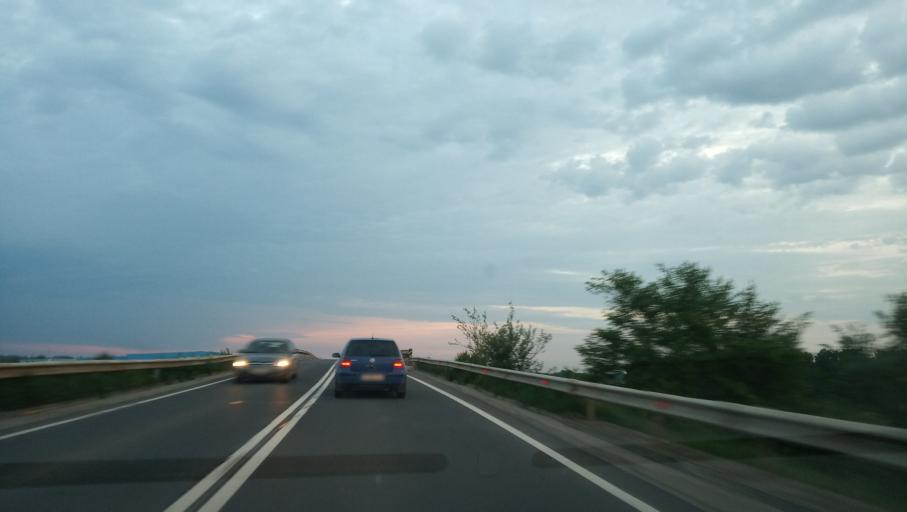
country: RO
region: Timis
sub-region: Comuna Sag
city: Sag
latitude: 45.6259
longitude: 21.1912
